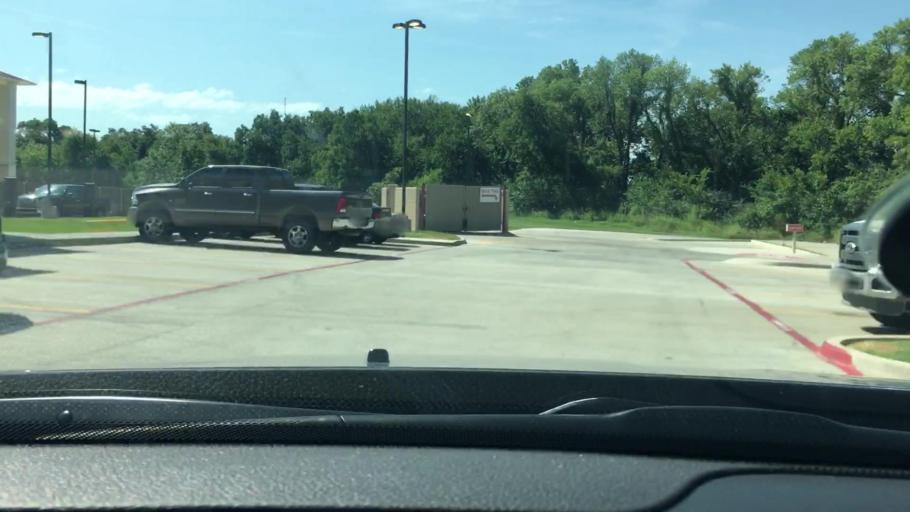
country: US
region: Oklahoma
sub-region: Carter County
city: Ardmore
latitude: 34.1870
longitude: -97.1630
